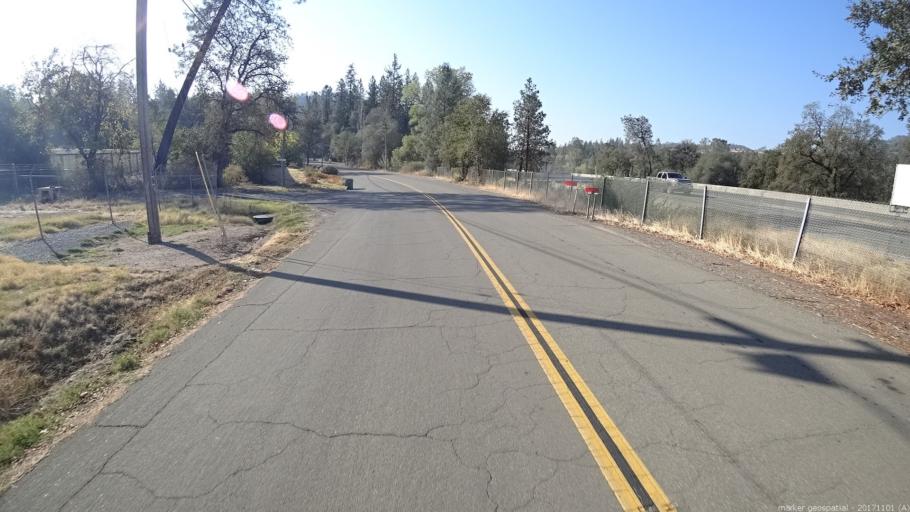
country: US
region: California
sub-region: Shasta County
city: Shasta Lake
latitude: 40.7290
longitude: -122.3207
